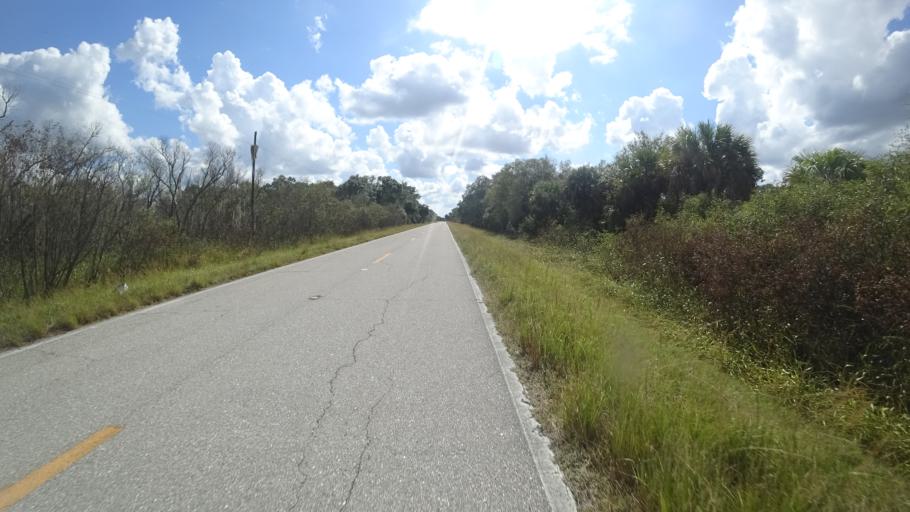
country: US
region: Florida
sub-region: Sarasota County
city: North Port
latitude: 27.2411
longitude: -82.1219
